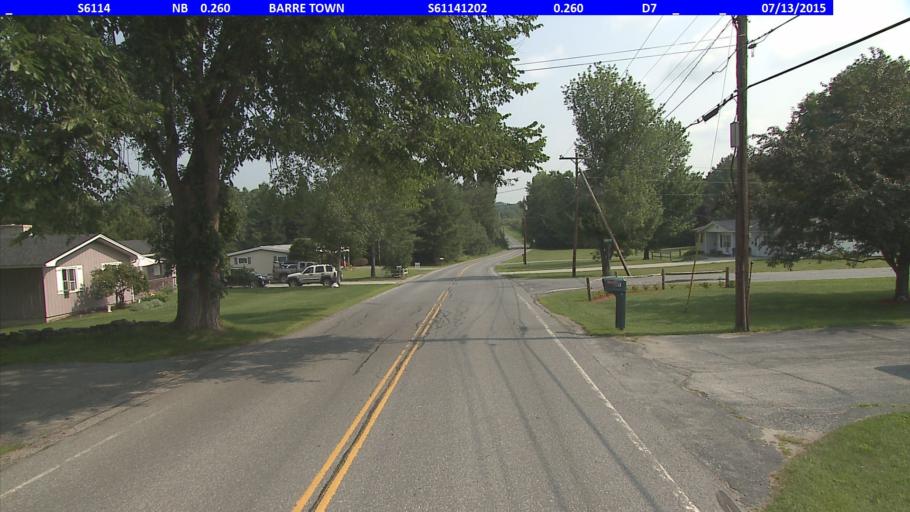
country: US
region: Vermont
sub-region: Washington County
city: Barre
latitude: 44.1954
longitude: -72.4792
